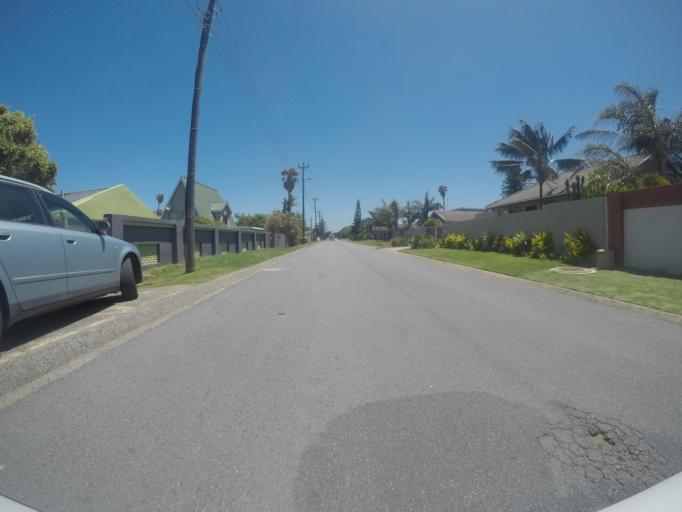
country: ZA
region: Eastern Cape
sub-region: Buffalo City Metropolitan Municipality
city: East London
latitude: -32.9522
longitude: 28.0094
